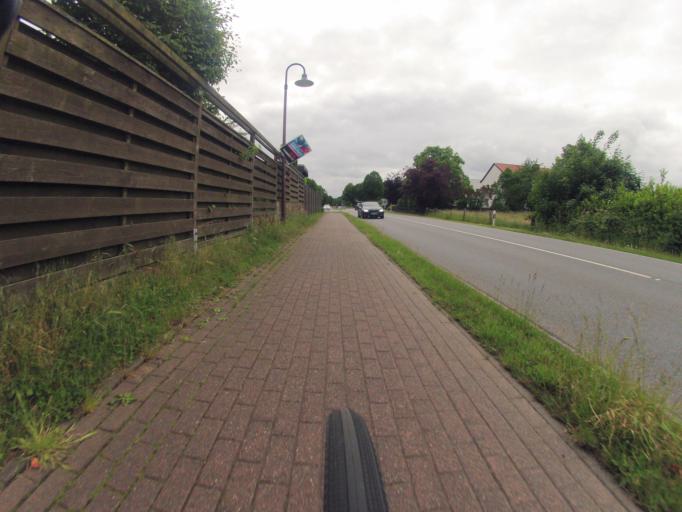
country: DE
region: North Rhine-Westphalia
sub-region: Regierungsbezirk Munster
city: Saerbeck
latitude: 52.1750
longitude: 7.6215
